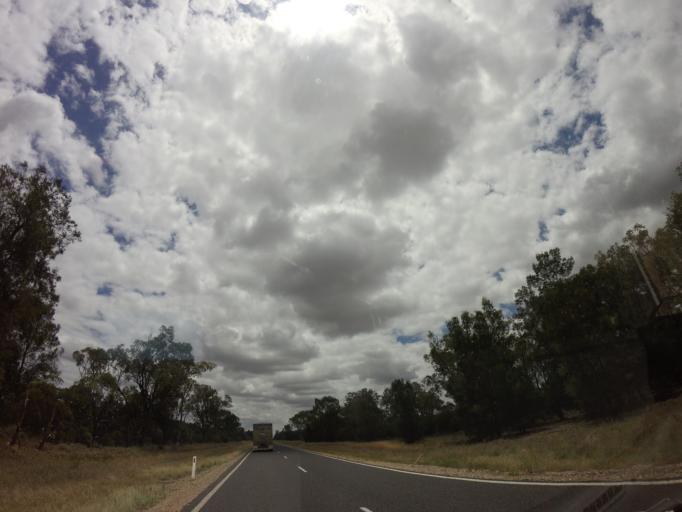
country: AU
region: Queensland
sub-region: Goondiwindi
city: Goondiwindi
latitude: -28.4301
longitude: 150.3021
